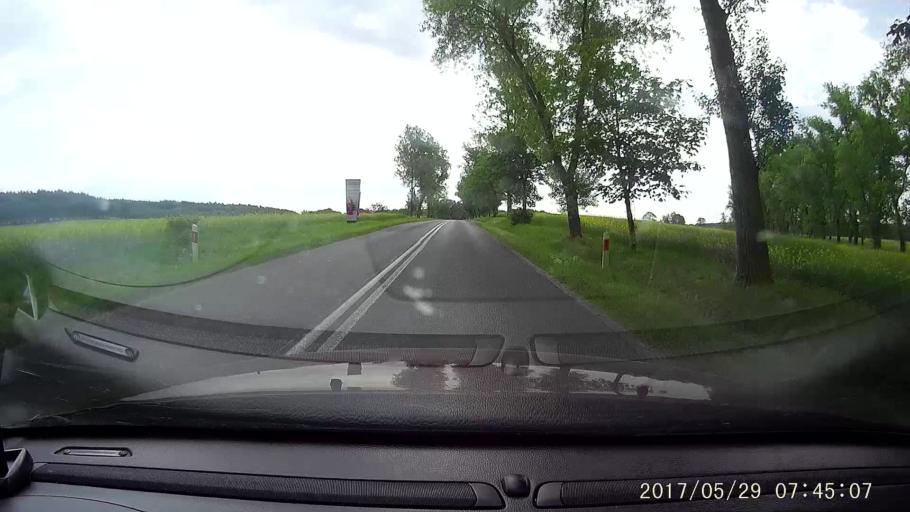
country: PL
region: Lower Silesian Voivodeship
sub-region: Powiat boleslawiecki
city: Boleslawiec
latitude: 51.2385
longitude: 15.6181
